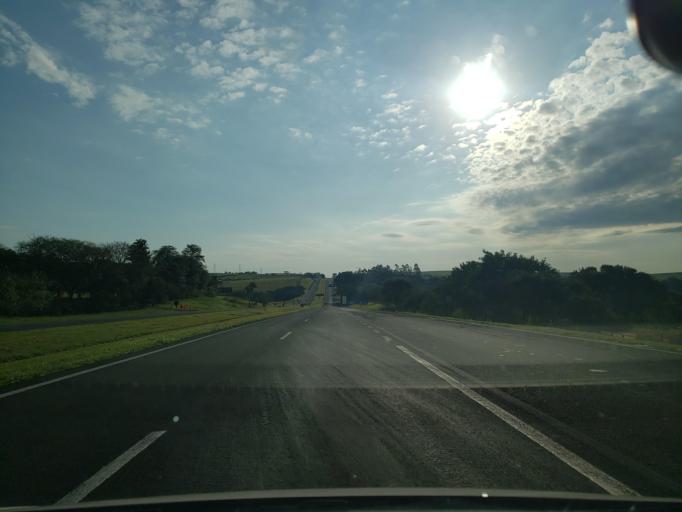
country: BR
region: Sao Paulo
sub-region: Valparaiso
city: Valparaiso
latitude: -21.2110
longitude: -50.8696
